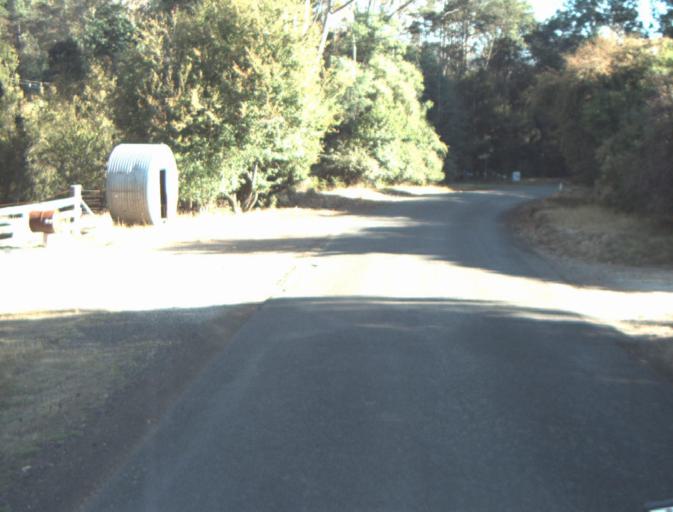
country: AU
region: Tasmania
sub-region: Launceston
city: Mayfield
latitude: -41.3041
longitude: 147.1982
